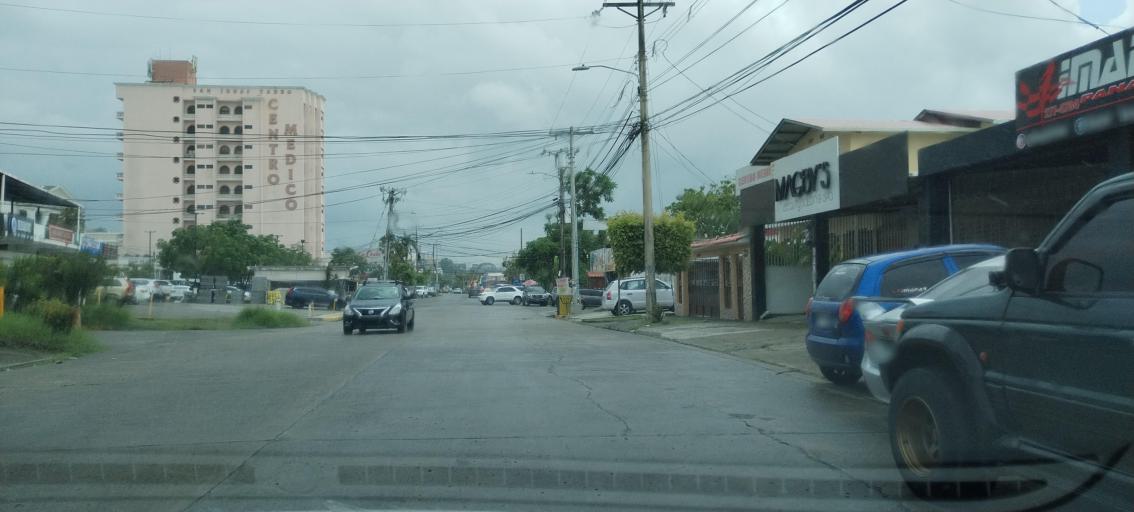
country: PA
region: Panama
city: San Miguelito
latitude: 9.0366
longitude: -79.4840
